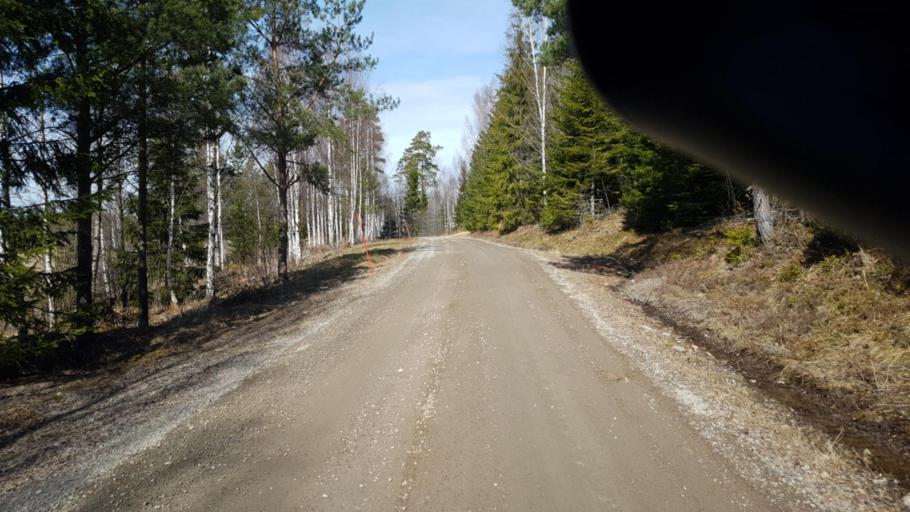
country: SE
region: Vaermland
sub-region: Grums Kommun
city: Grums
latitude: 59.5244
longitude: 12.9203
